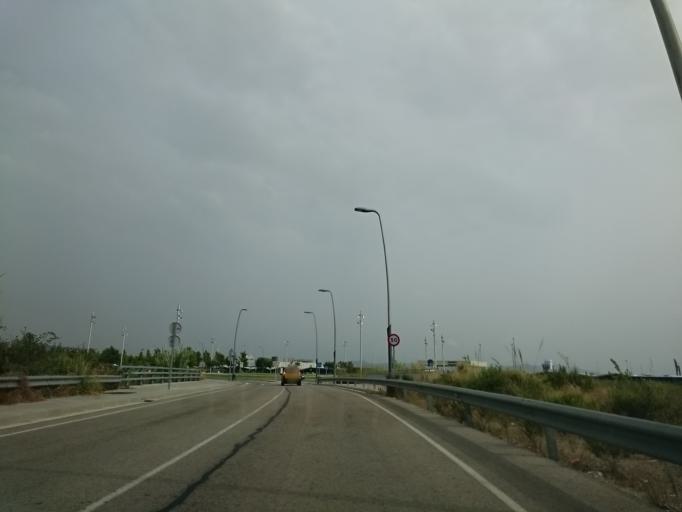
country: ES
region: Catalonia
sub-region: Provincia de Barcelona
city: Viladecans
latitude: 41.2902
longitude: 2.0553
